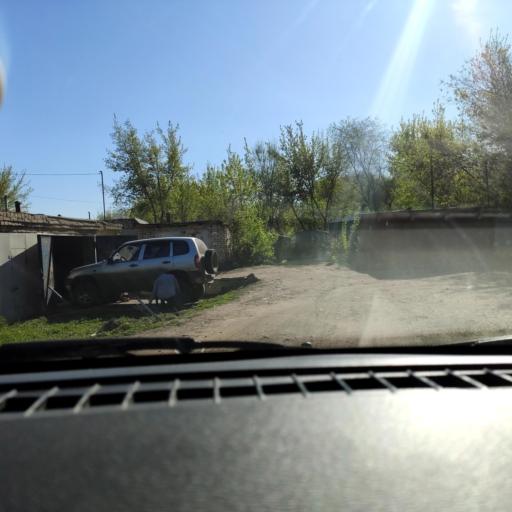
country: RU
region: Samara
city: Samara
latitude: 53.2063
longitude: 50.2499
